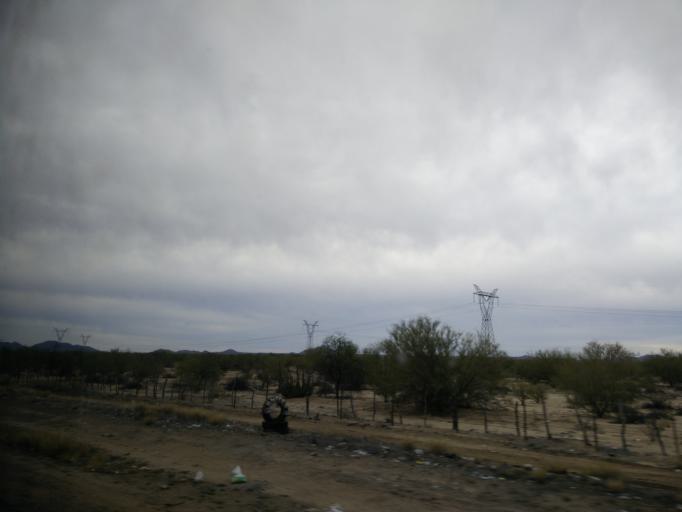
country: MX
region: Sonora
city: Hermosillo
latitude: 28.6878
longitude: -110.9905
